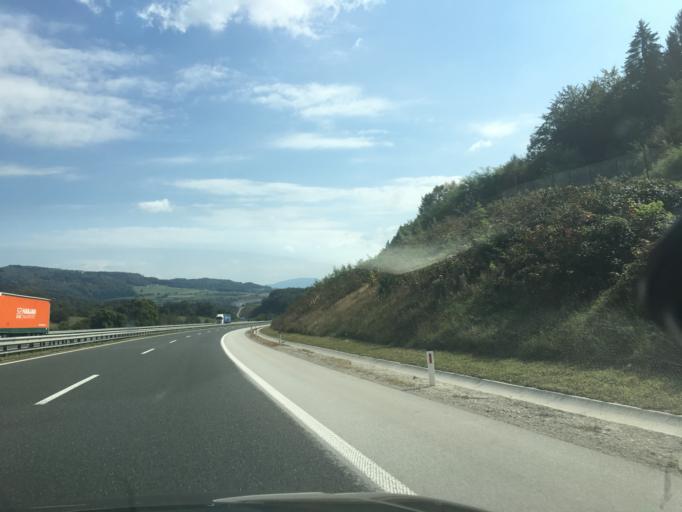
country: SI
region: Mirna Pec
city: Mirna Pec
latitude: 45.8730
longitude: 15.1076
